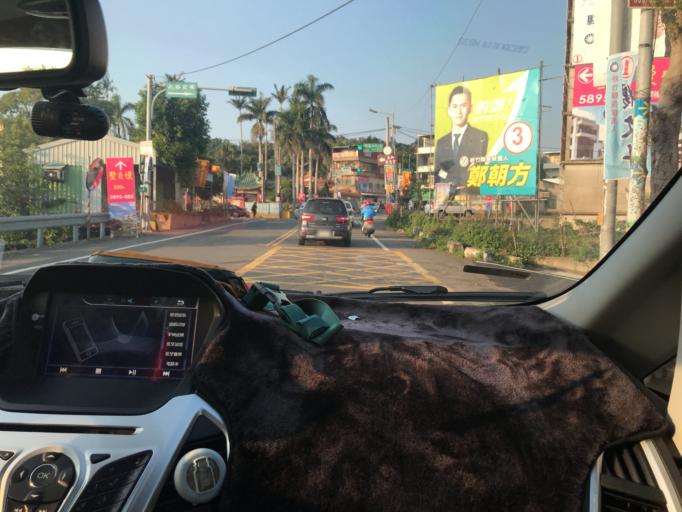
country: TW
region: Taiwan
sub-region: Hsinchu
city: Zhubei
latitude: 24.8426
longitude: 121.0367
